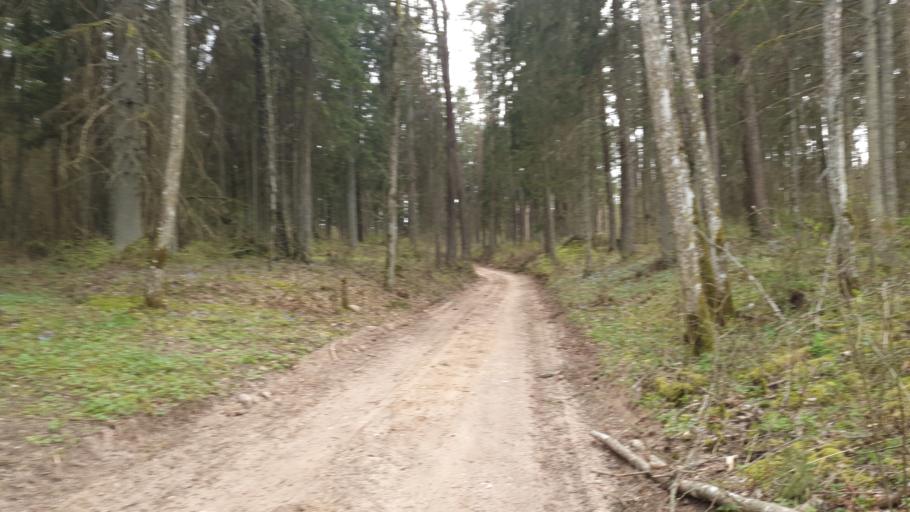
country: LT
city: Aukstadvaris
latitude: 54.5105
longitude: 24.6370
